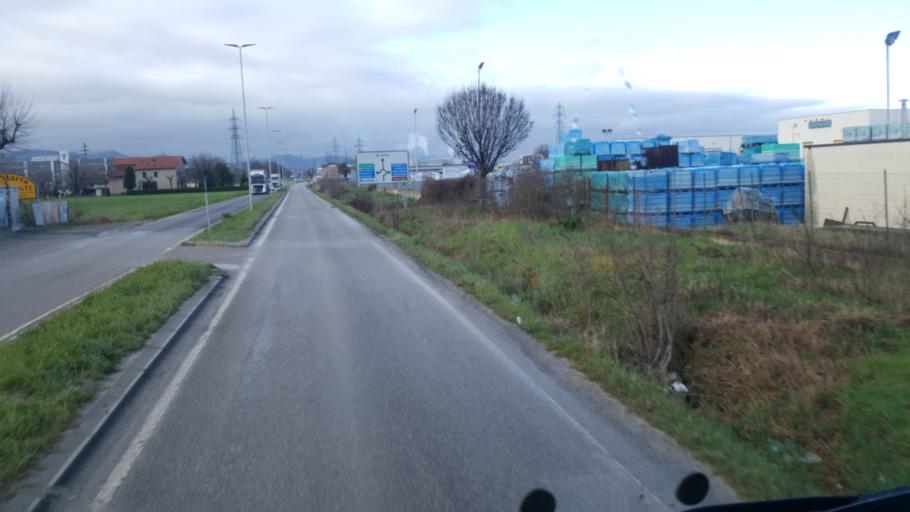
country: IT
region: Emilia-Romagna
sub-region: Provincia di Modena
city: Sassuolo
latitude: 44.5607
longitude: 10.7896
